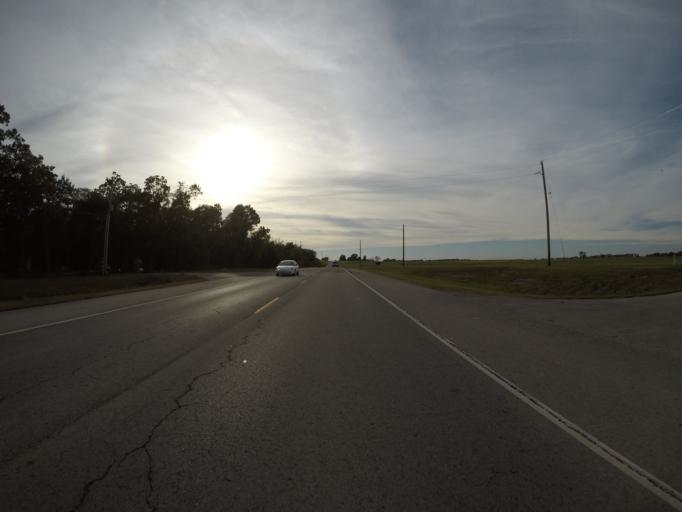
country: US
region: Kansas
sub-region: Douglas County
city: Baldwin City
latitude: 38.7823
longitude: -95.2204
